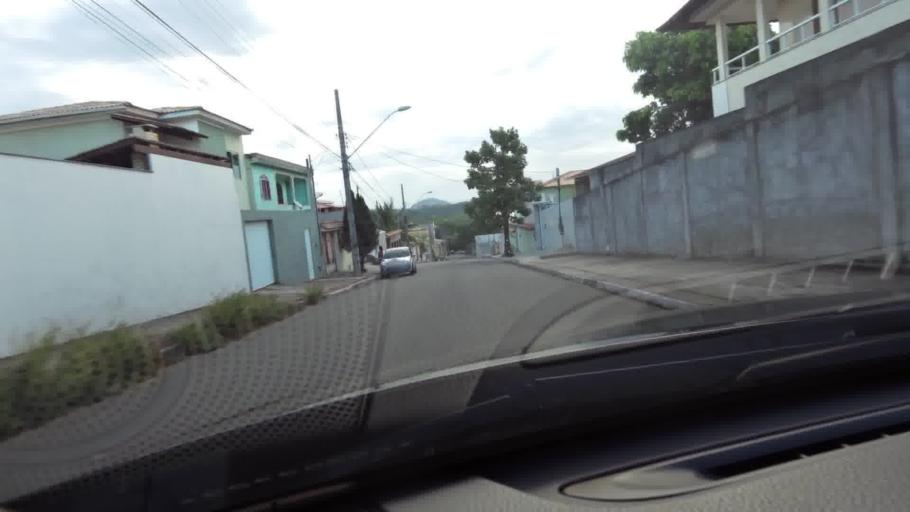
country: BR
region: Espirito Santo
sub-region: Guarapari
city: Guarapari
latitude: -20.6636
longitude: -40.5115
